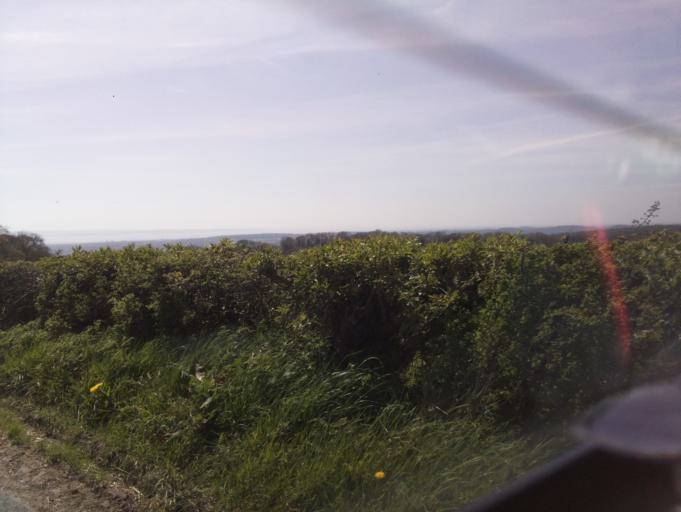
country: GB
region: Wales
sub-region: Newport
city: Llanvaches
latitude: 51.6426
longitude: -2.7683
